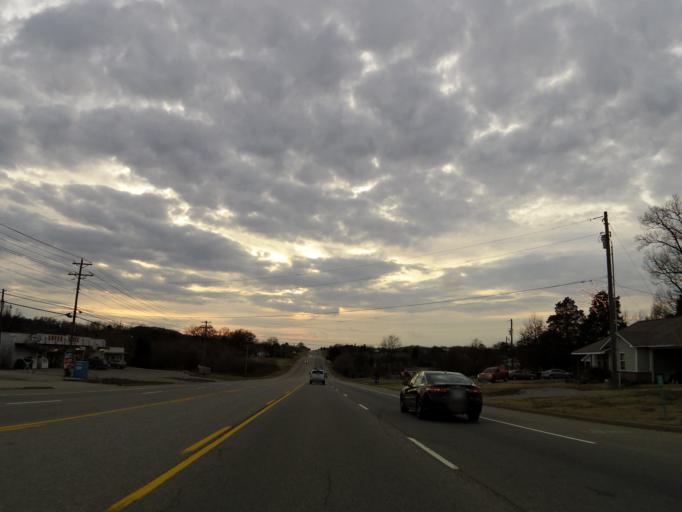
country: US
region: Tennessee
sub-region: Loudon County
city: Greenback
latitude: 35.6409
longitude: -84.1514
